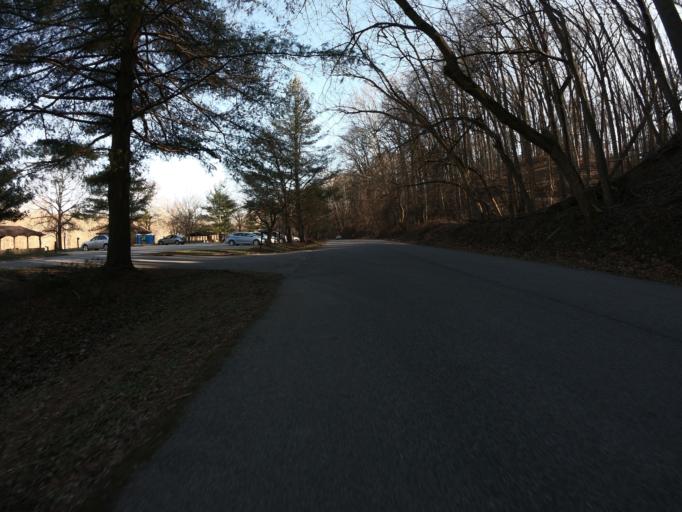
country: US
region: Maryland
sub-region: Howard County
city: Elkridge
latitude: 39.2274
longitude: -76.7260
